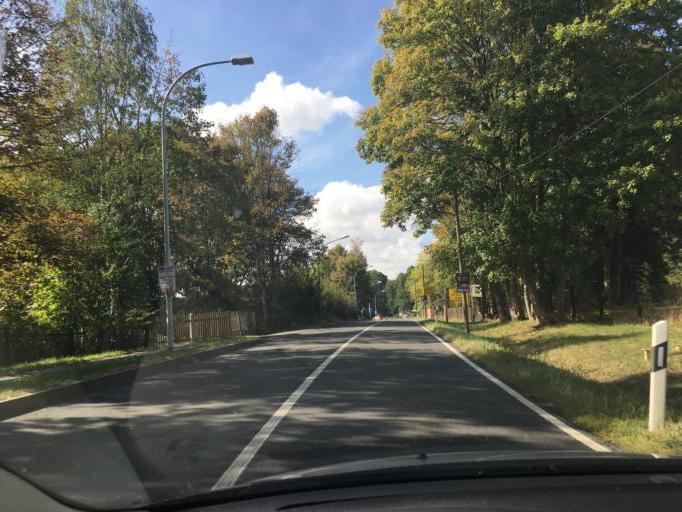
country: DE
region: Thuringia
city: Auma
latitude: 50.7060
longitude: 11.8970
